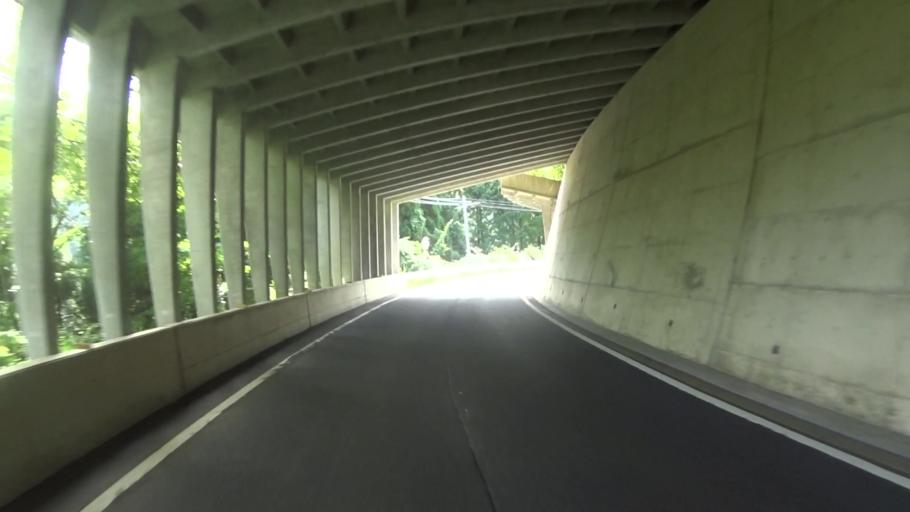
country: JP
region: Kyoto
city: Miyazu
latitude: 35.7024
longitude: 135.1867
